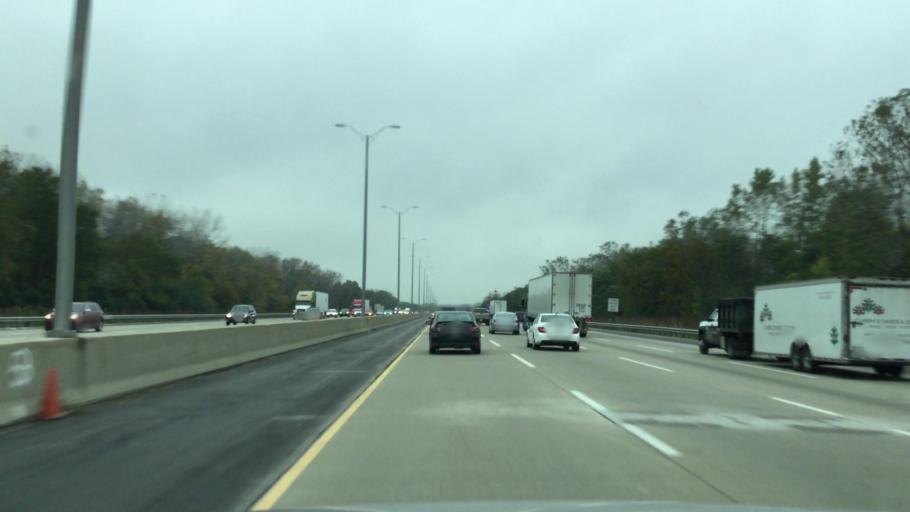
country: US
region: Illinois
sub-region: Lake County
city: Lincolnshire
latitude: 42.2129
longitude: -87.8945
